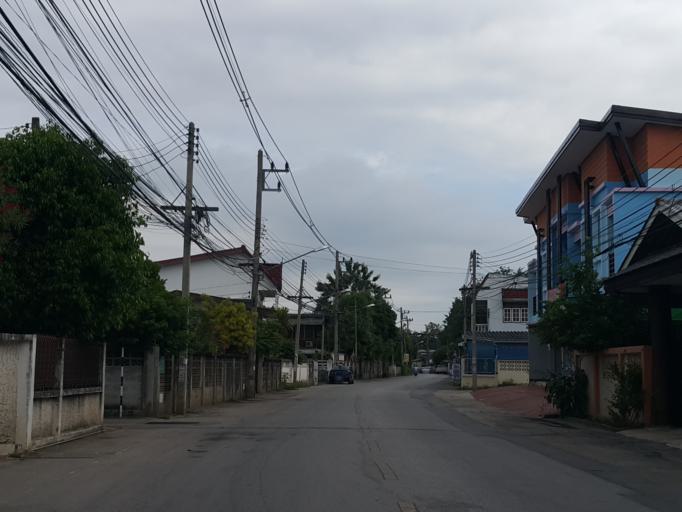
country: TH
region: Lampang
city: Lampang
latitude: 18.2969
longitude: 99.5028
